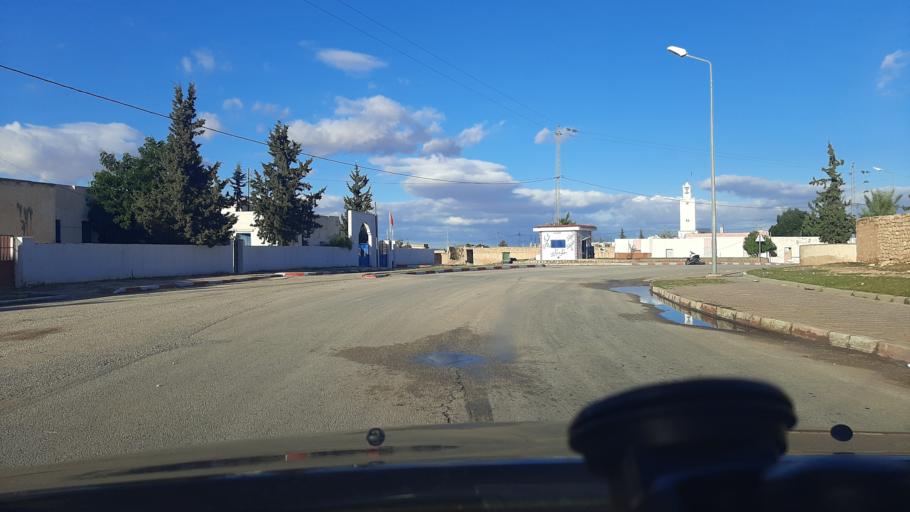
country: TN
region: Al Mahdiyah
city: Shurban
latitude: 34.9605
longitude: 10.3624
